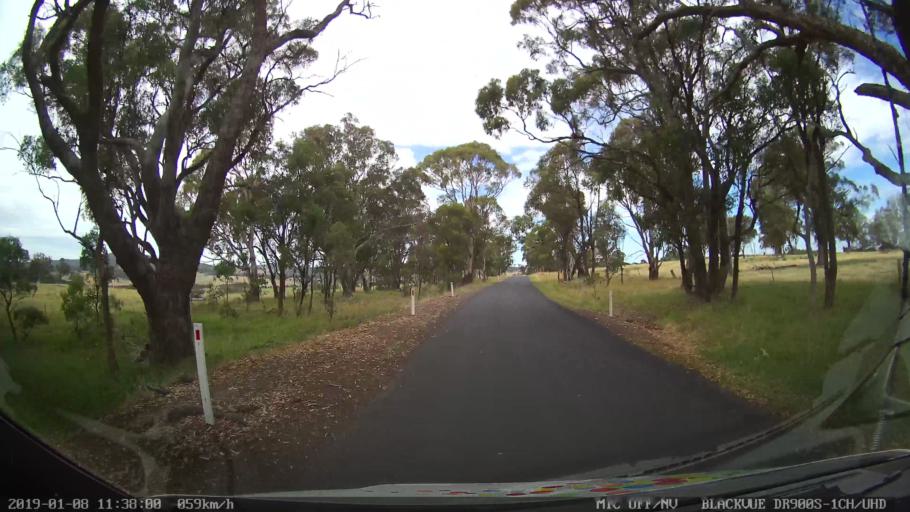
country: AU
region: New South Wales
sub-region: Guyra
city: Guyra
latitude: -30.3565
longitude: 151.5551
